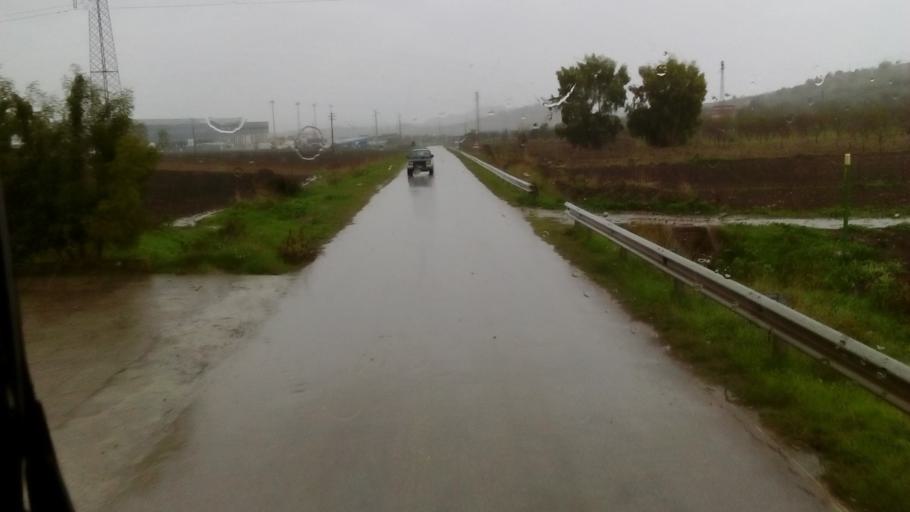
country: IT
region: Sicily
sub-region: Enna
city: Pietraperzia
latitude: 37.4075
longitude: 14.1418
